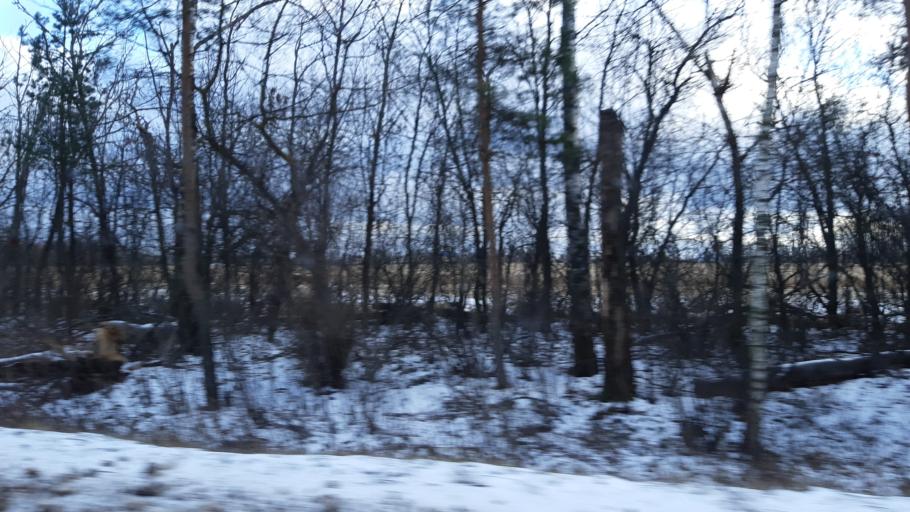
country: RU
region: Moskovskaya
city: Noginsk-9
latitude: 56.0018
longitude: 38.5502
